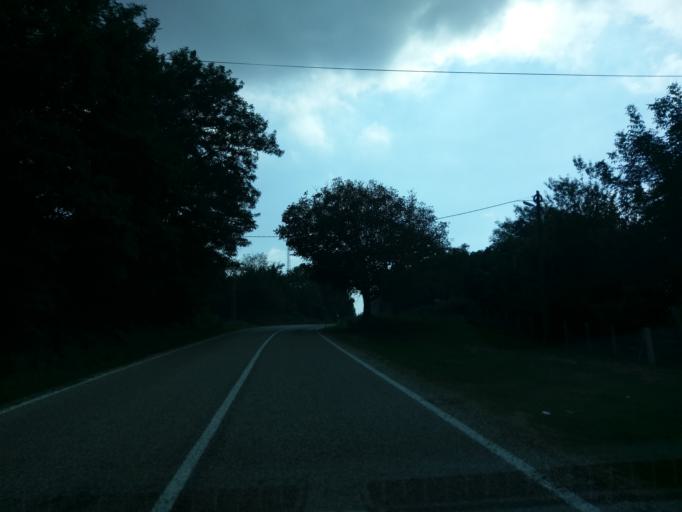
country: TR
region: Sinop
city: Erfelek
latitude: 41.9830
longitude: 34.8780
